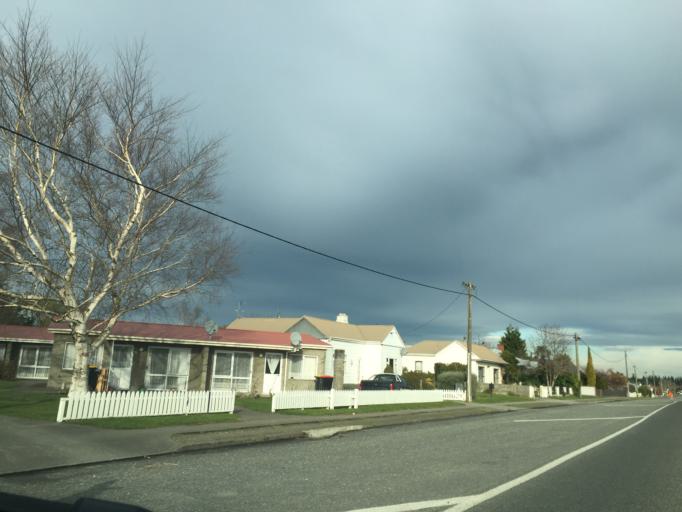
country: NZ
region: Southland
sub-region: Gore District
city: Gore
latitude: -46.1974
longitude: 168.8596
